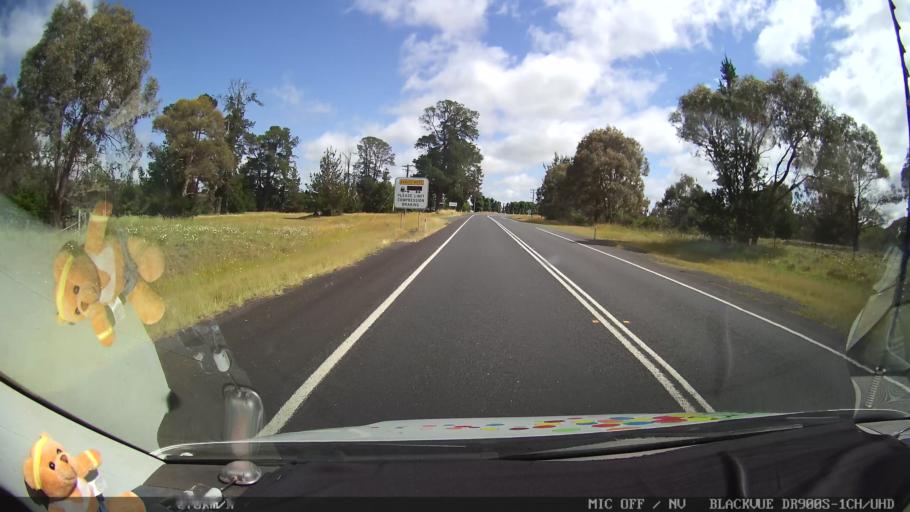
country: AU
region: New South Wales
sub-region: Glen Innes Severn
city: Glen Innes
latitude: -29.9319
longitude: 151.7237
